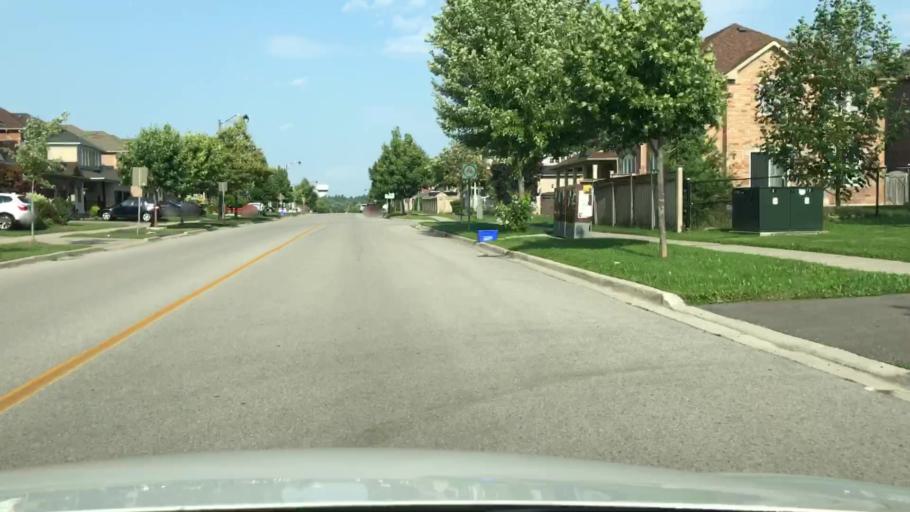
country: CA
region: Ontario
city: Newmarket
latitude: 44.0131
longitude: -79.4405
